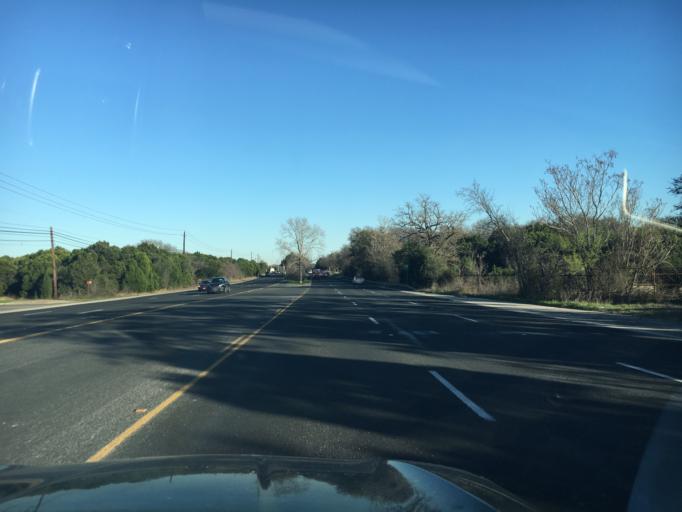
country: US
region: Texas
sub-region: Travis County
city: Barton Creek
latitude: 30.2420
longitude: -97.8379
